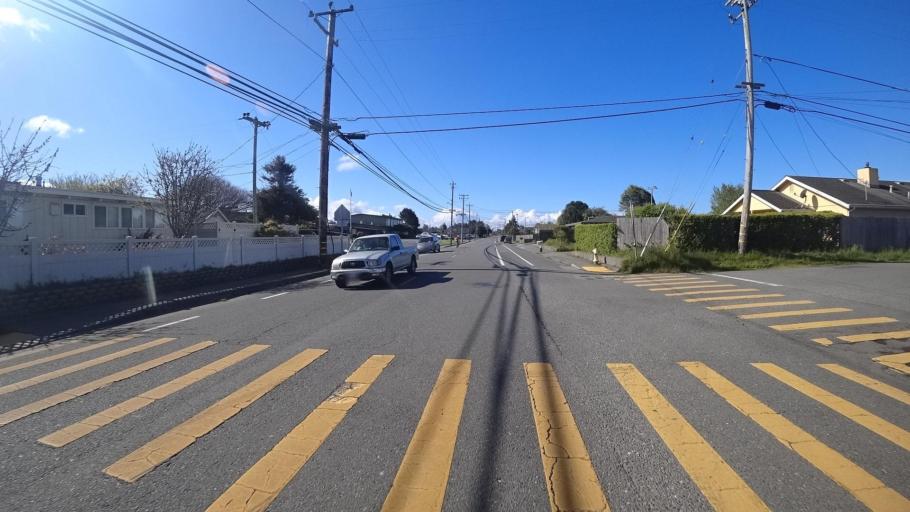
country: US
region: California
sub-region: Humboldt County
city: McKinleyville
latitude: 40.9509
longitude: -124.1102
